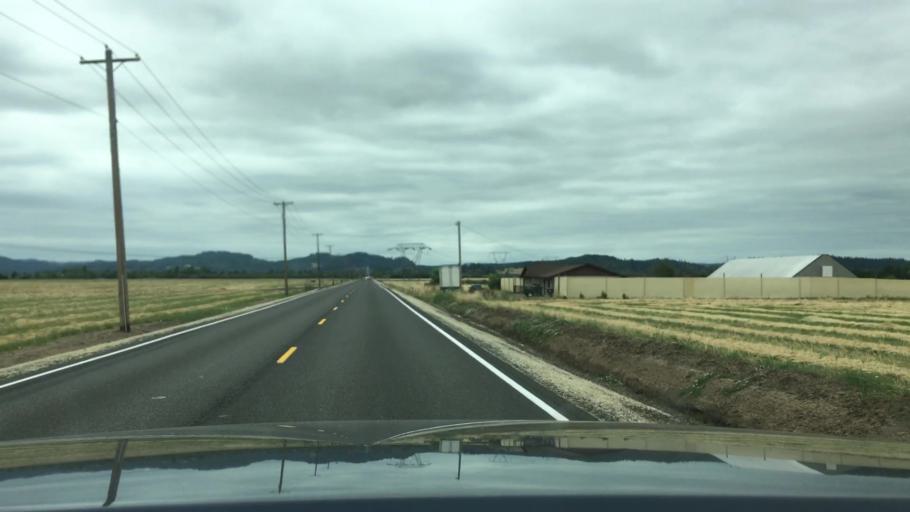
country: US
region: Oregon
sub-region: Lane County
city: Junction City
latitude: 44.0971
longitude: -123.2084
